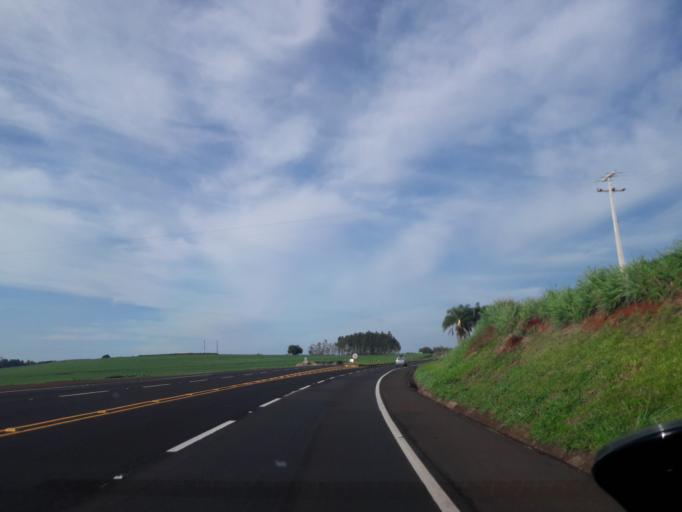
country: BR
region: Parana
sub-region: Mandaguari
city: Mandaguari
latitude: -23.4666
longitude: -51.5728
